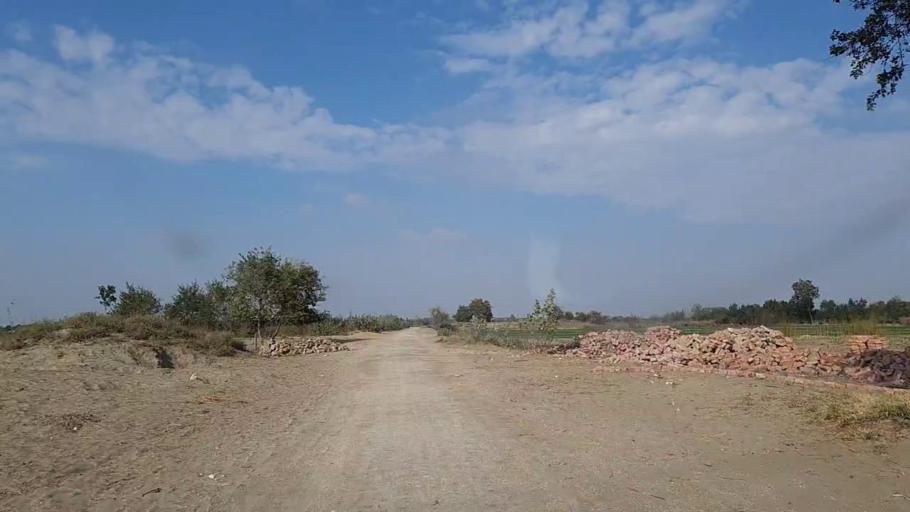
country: PK
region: Sindh
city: Sanghar
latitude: 26.2700
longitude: 69.0121
